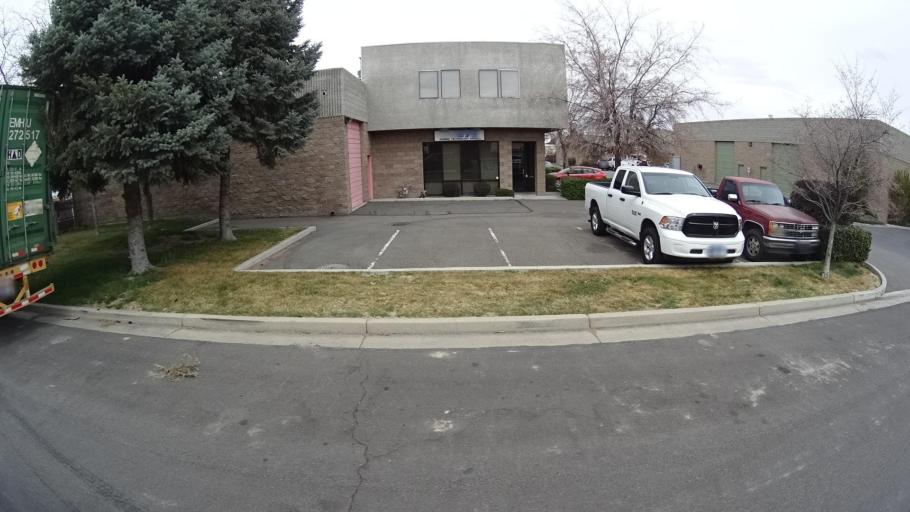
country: US
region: Nevada
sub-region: Washoe County
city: Sparks
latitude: 39.5236
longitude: -119.7348
